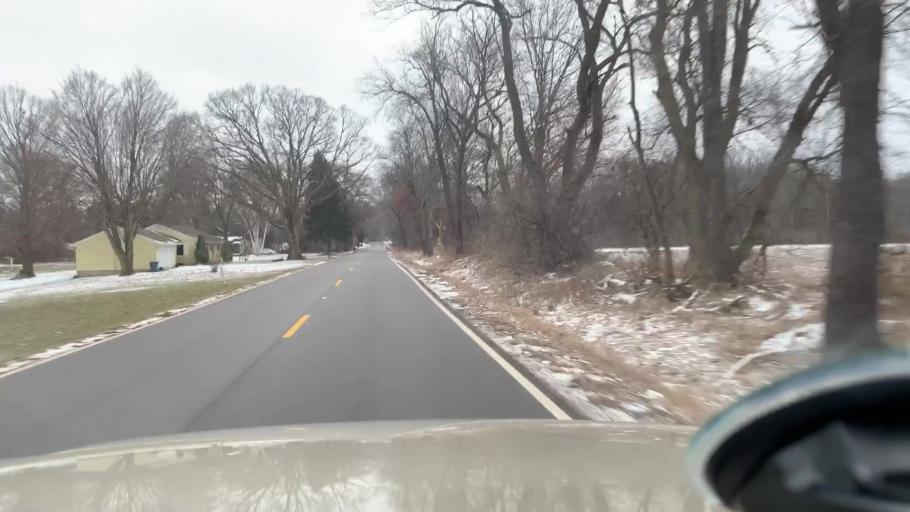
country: US
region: Michigan
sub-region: Jackson County
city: Spring Arbor
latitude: 42.2055
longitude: -84.5309
